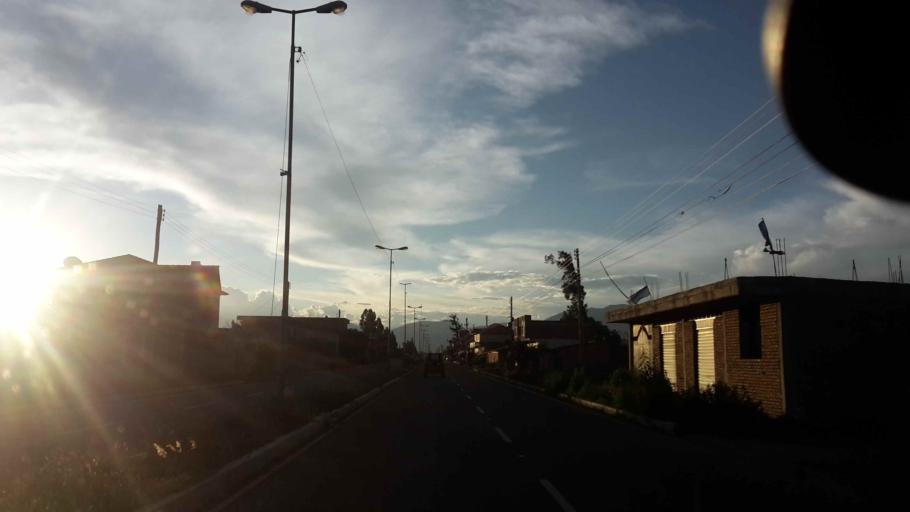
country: BO
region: Cochabamba
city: Arani
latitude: -17.5601
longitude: -65.8004
